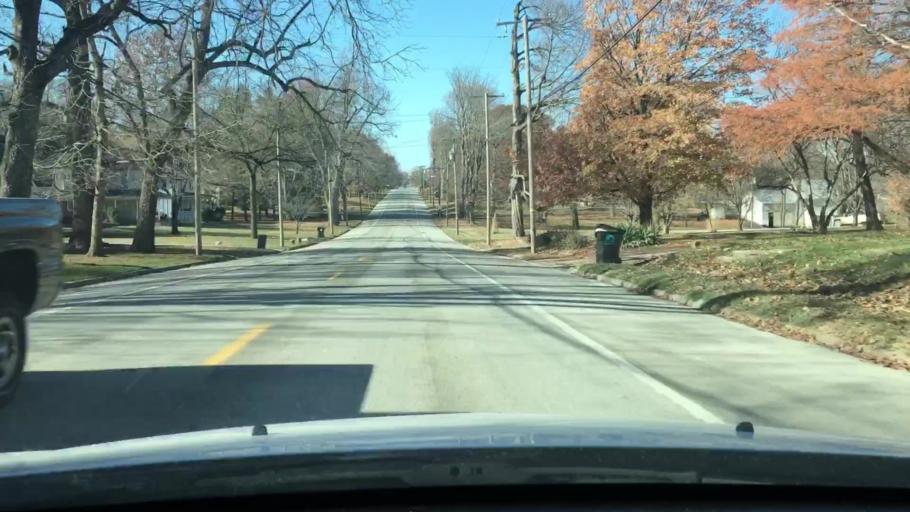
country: US
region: Illinois
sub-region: Pike County
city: Pittsfield
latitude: 39.6068
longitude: -90.7950
